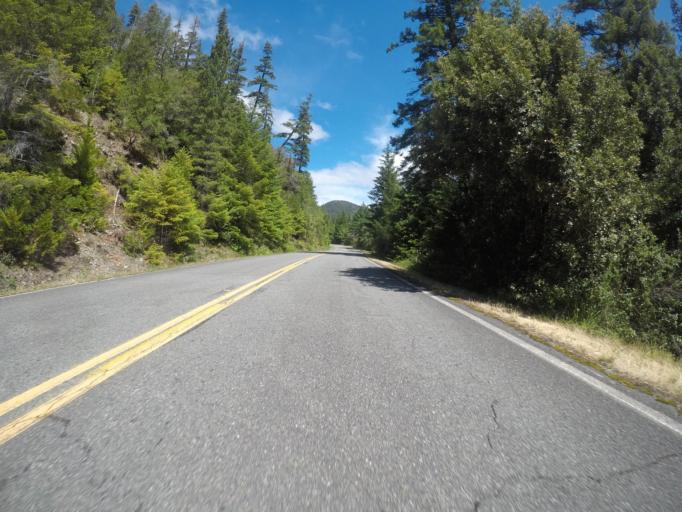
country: US
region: California
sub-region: Del Norte County
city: Bertsch-Oceanview
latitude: 41.7093
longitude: -123.9417
